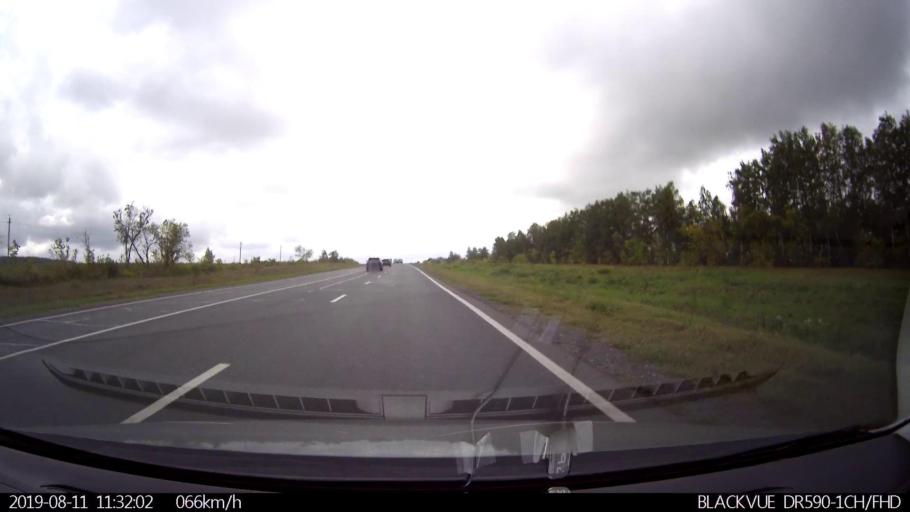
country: RU
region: Ulyanovsk
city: Krasnyy Gulyay
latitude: 54.0414
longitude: 48.2141
